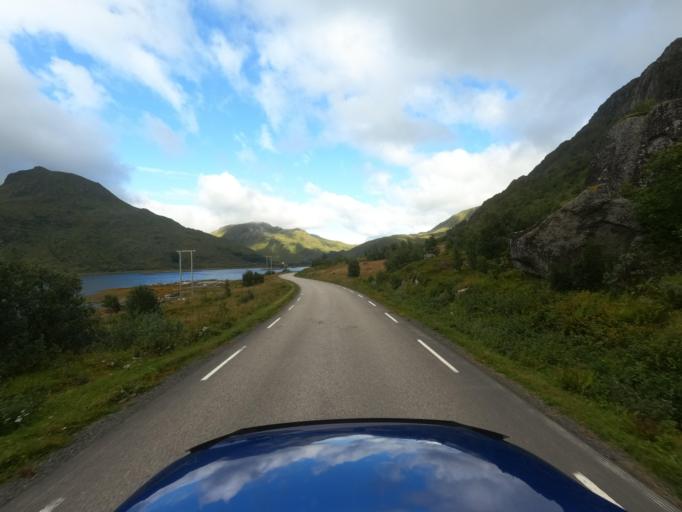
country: NO
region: Nordland
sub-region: Vestvagoy
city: Evjen
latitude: 68.1866
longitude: 13.8928
